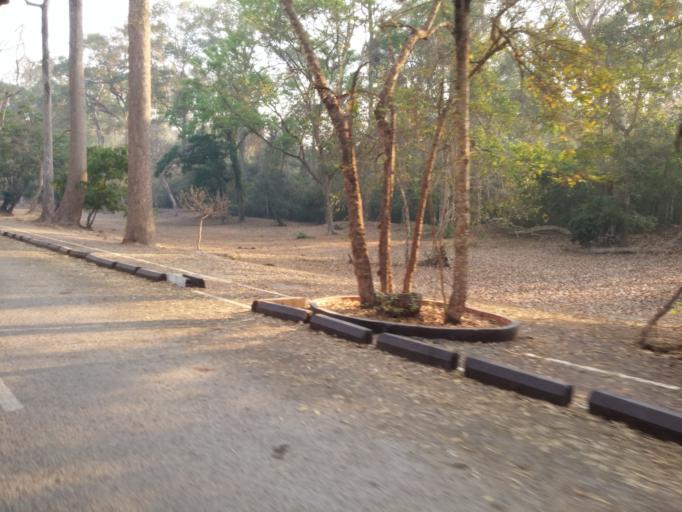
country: KH
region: Siem Reap
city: Siem Reap
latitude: 13.4285
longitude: 103.8595
